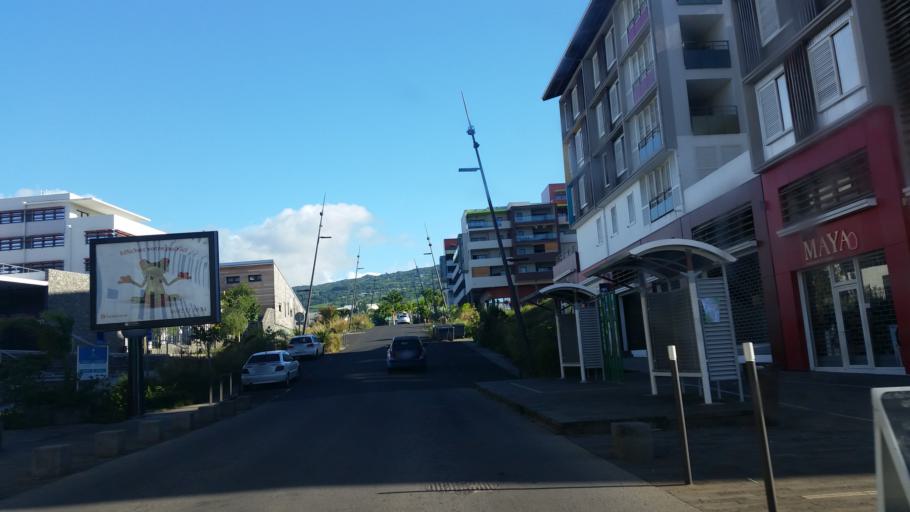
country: RE
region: Reunion
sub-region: Reunion
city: Sainte-Marie
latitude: -20.9208
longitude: 55.5287
